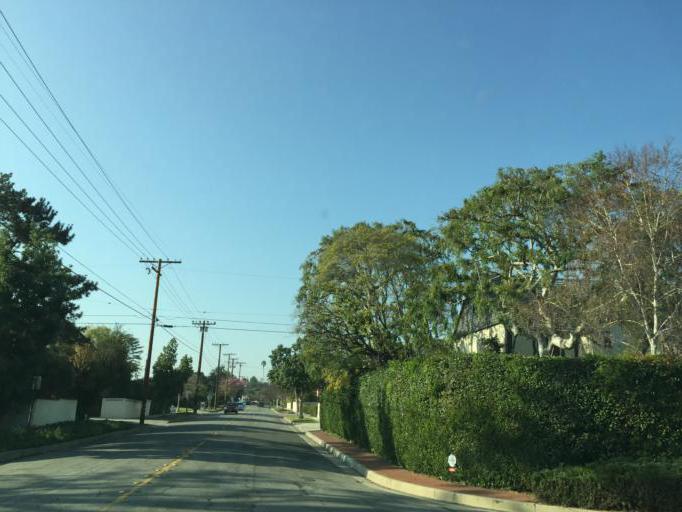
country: US
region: California
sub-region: Los Angeles County
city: South Pasadena
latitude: 34.1136
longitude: -118.1342
